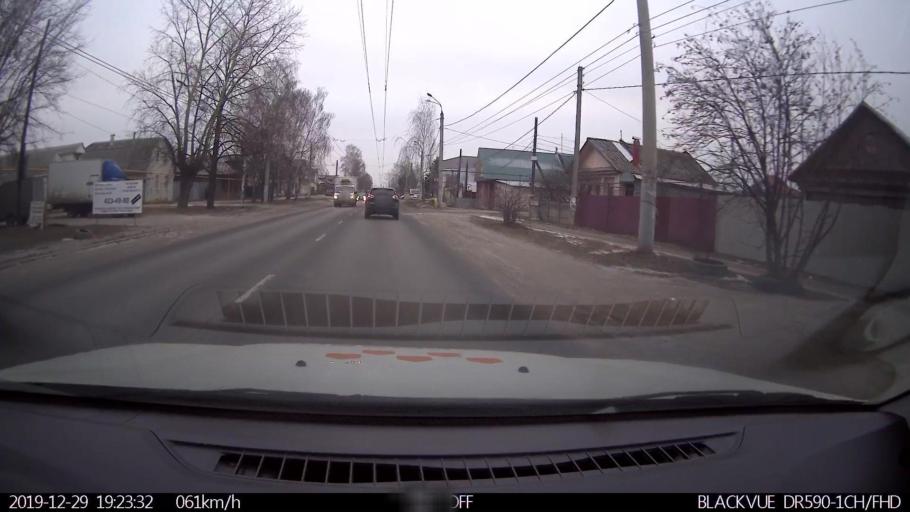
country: RU
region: Nizjnij Novgorod
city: Gorbatovka
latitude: 56.3809
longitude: 43.8076
